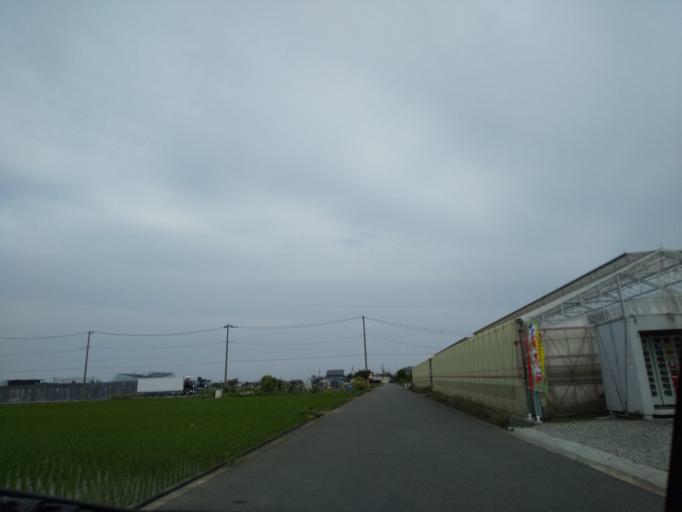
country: JP
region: Kanagawa
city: Zama
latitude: 35.4823
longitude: 139.3530
